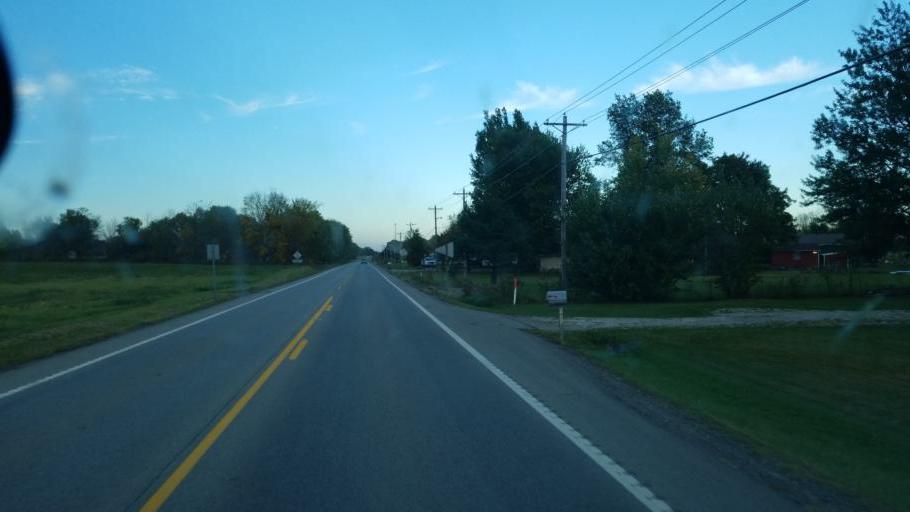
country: US
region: Ohio
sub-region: Licking County
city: Johnstown
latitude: 40.1942
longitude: -82.5975
